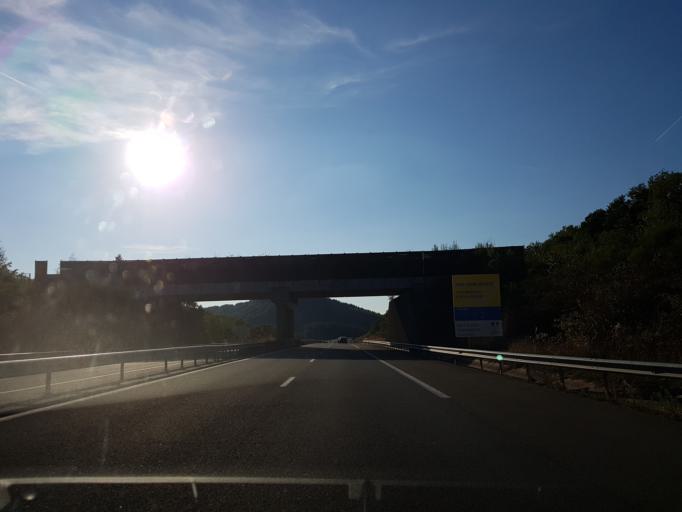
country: FR
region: Franche-Comte
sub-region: Departement de la Haute-Saone
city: Ronchamp
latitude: 47.6222
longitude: 6.6590
